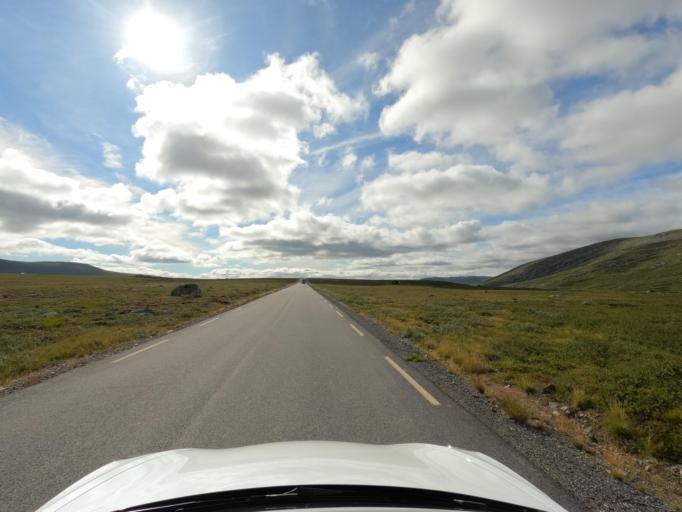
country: NO
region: Telemark
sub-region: Tinn
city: Rjukan
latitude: 60.1739
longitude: 8.5910
